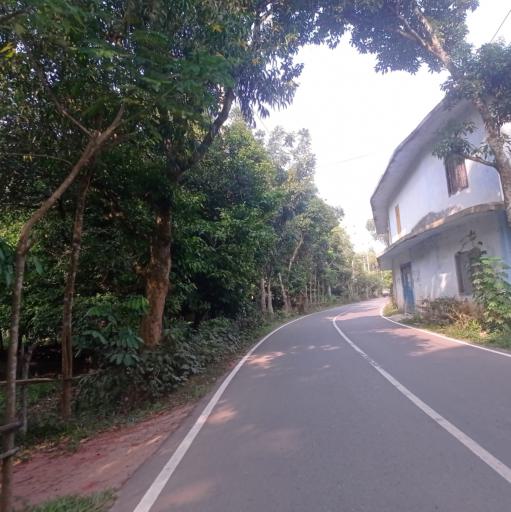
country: BD
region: Dhaka
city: Bhairab Bazar
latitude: 24.0709
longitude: 90.8425
